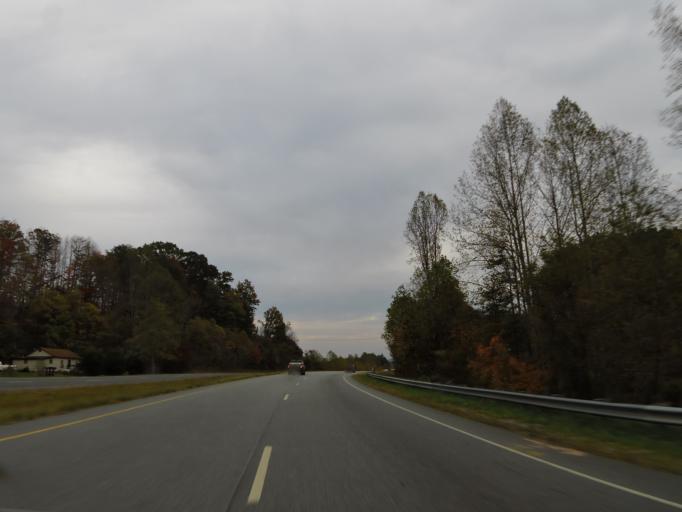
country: US
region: North Carolina
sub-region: Caldwell County
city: Lenoir
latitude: 35.9568
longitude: -81.5608
